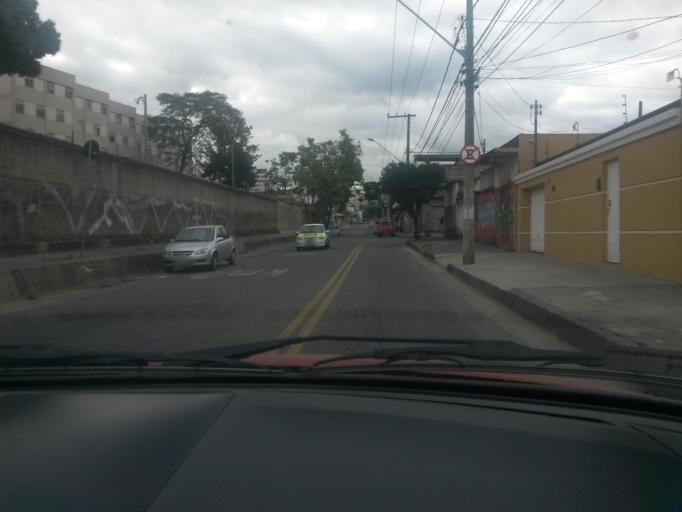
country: BR
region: Minas Gerais
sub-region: Belo Horizonte
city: Belo Horizonte
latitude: -19.9105
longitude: -43.9745
